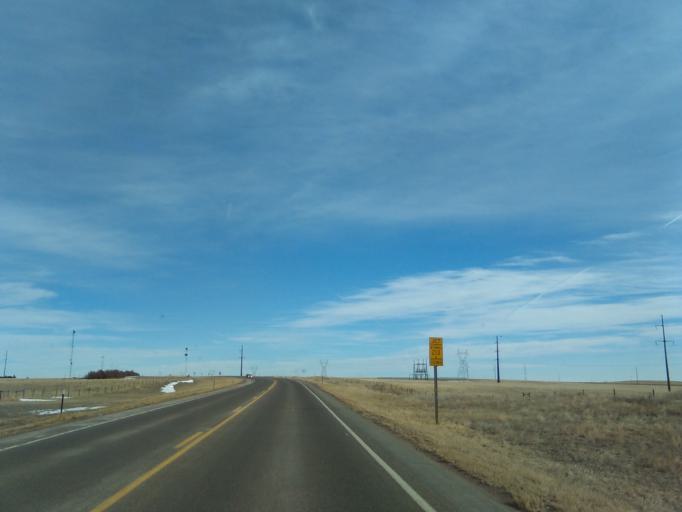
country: US
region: Wyoming
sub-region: Laramie County
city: Pine Bluffs
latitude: 41.4373
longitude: -104.3545
